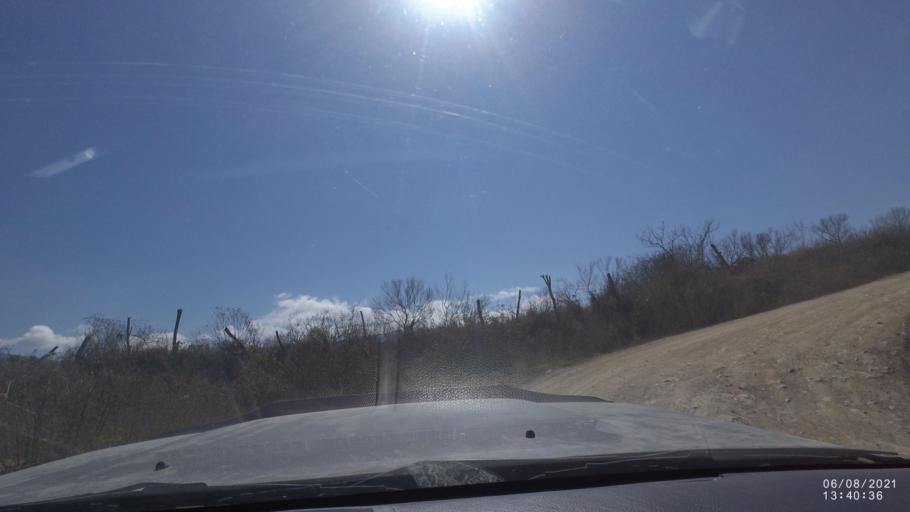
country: BO
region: La Paz
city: Quime
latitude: -16.6851
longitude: -66.7335
